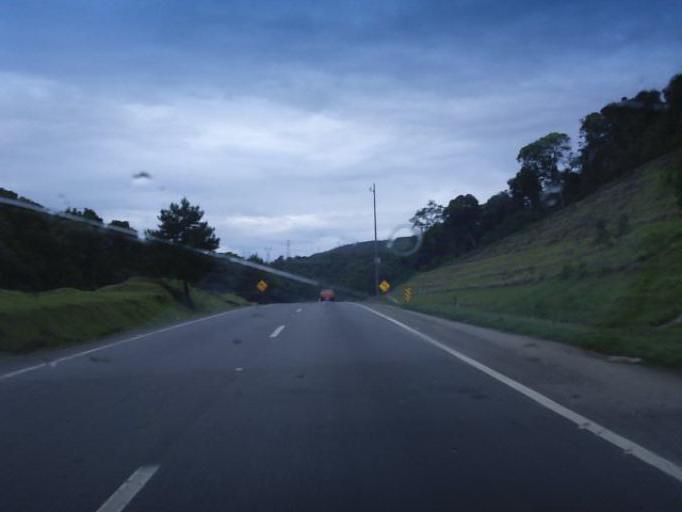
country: BR
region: Parana
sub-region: Sao Jose Dos Pinhais
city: Sao Jose dos Pinhais
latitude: -25.8544
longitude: -48.9867
